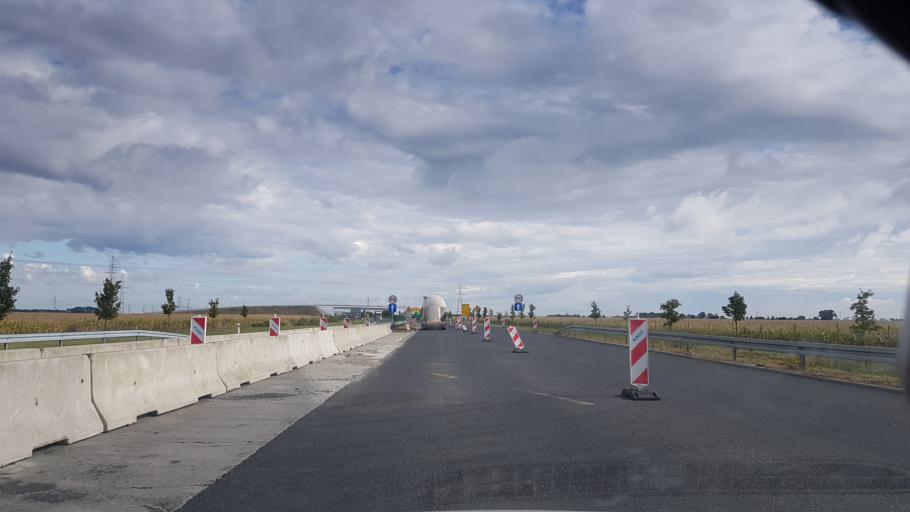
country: PL
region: Greater Poland Voivodeship
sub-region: Powiat poznanski
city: Komorniki
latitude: 52.3403
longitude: 16.7470
